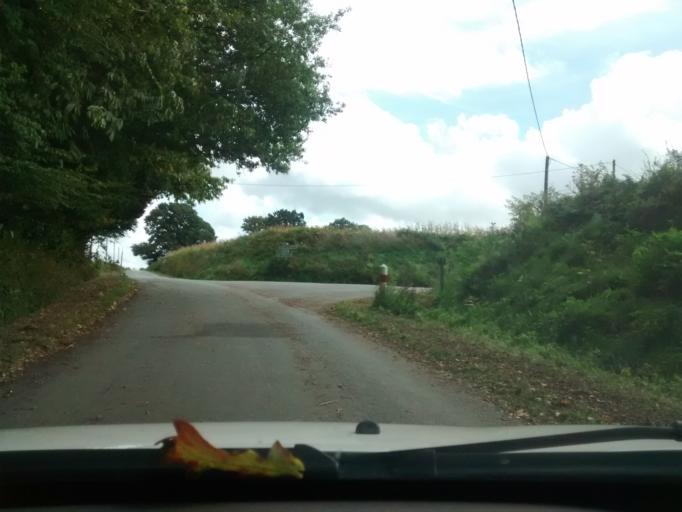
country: FR
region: Brittany
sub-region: Departement d'Ille-et-Vilaine
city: Chateaubourg
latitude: 48.1216
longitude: -1.3905
